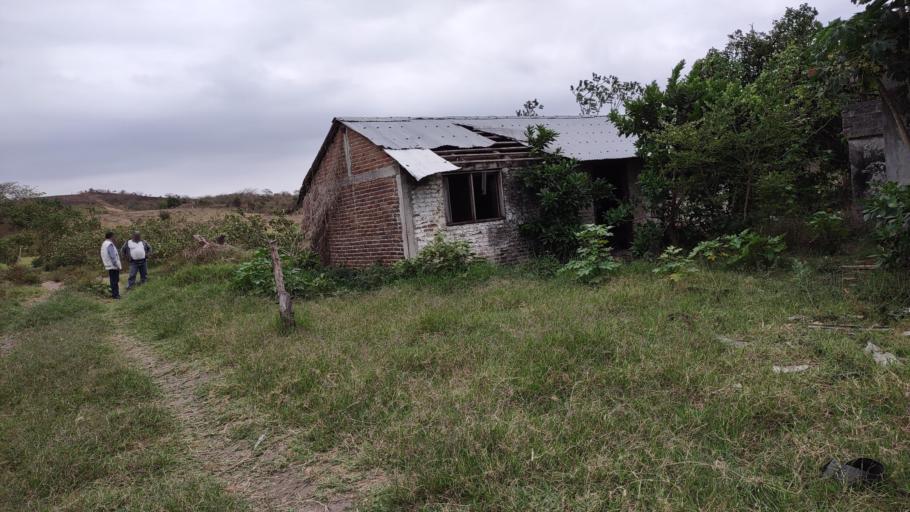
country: MX
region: Veracruz
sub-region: Veracruz
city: Delfino Victoria (Santa Fe)
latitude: 19.2696
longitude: -96.2999
